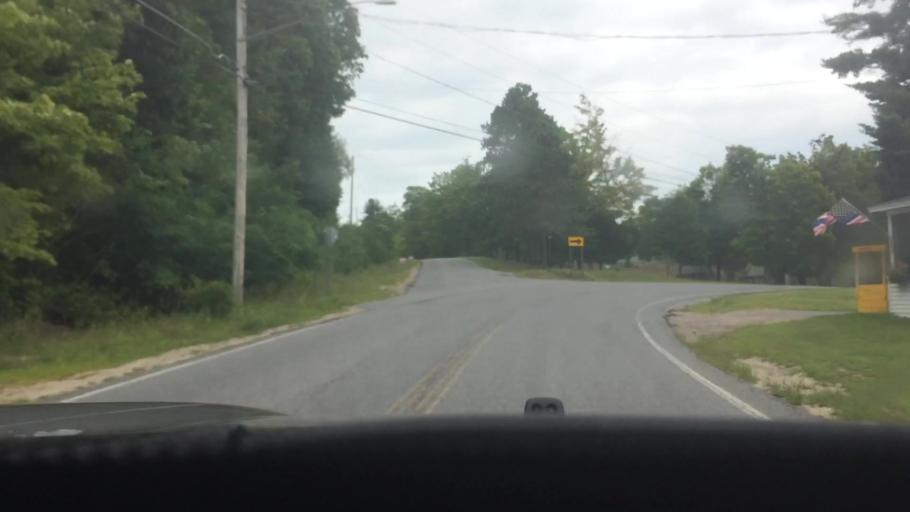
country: US
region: New York
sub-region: St. Lawrence County
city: Hannawa Falls
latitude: 44.5563
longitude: -74.9297
